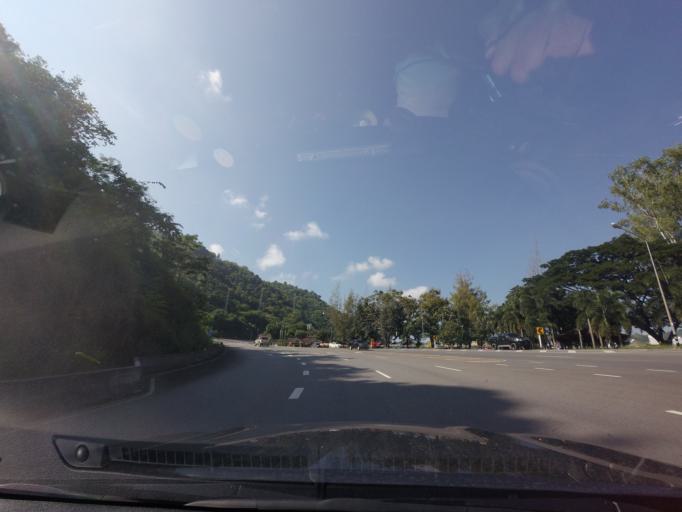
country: TH
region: Phetchabun
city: Khao Kho
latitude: 16.7826
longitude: 101.0845
